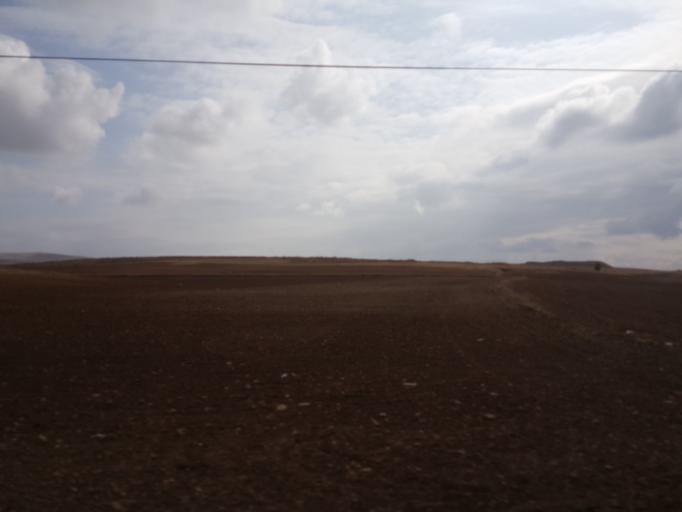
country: TR
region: Kirikkale
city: Keskin
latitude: 39.5844
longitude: 33.5984
